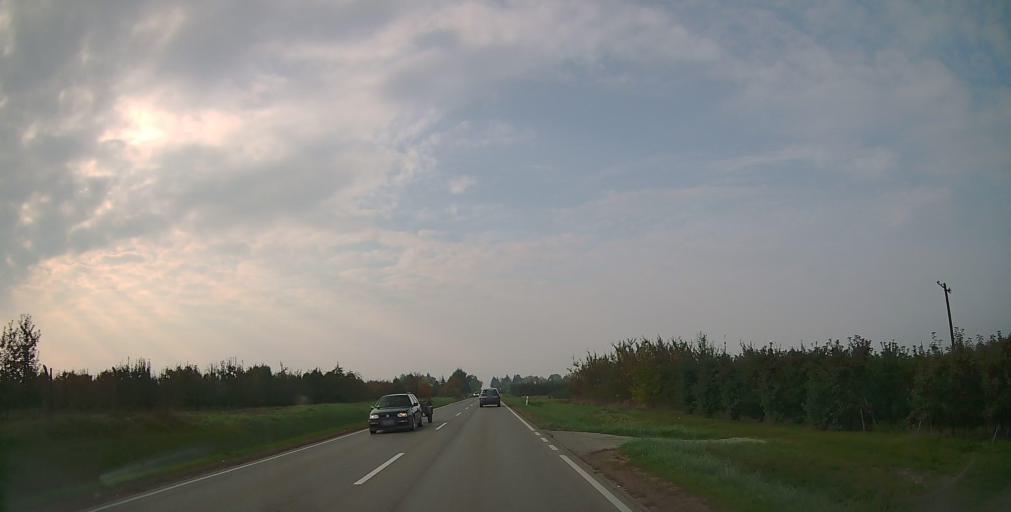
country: PL
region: Masovian Voivodeship
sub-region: Powiat grojecki
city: Belsk Duzy
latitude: 51.7825
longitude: 20.7756
